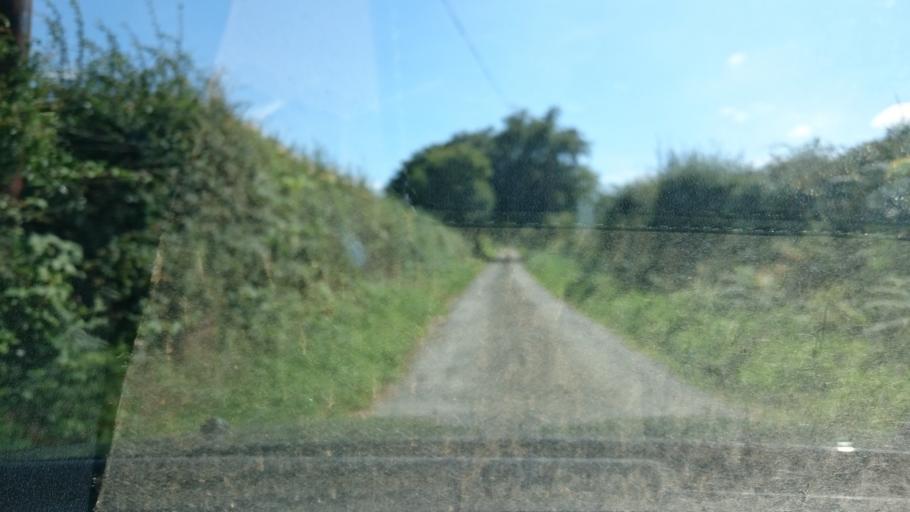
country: IE
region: Leinster
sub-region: Kilkenny
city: Graiguenamanagh
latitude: 52.5333
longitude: -6.9650
